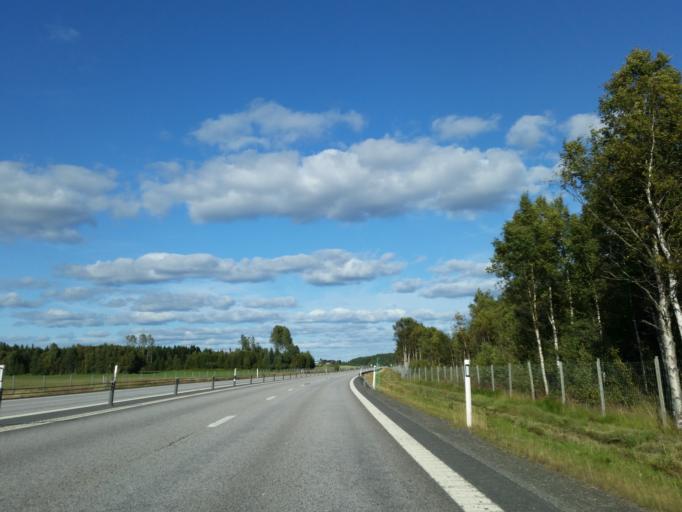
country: SE
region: Vaesterbotten
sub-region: Robertsfors Kommun
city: Robertsfors
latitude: 64.1441
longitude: 20.8981
